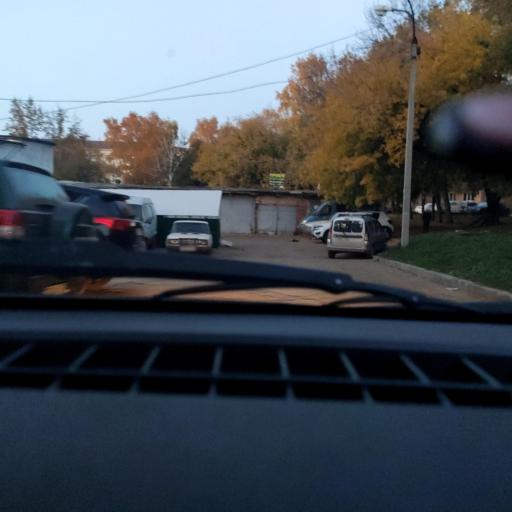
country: RU
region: Bashkortostan
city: Ufa
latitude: 54.7645
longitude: 56.0204
